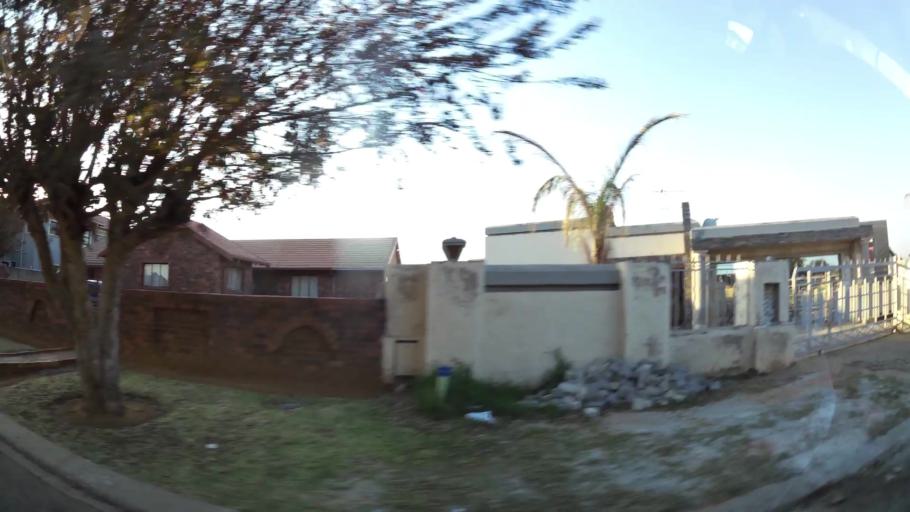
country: ZA
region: Gauteng
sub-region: West Rand District Municipality
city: Randfontein
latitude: -26.2049
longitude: 27.6533
